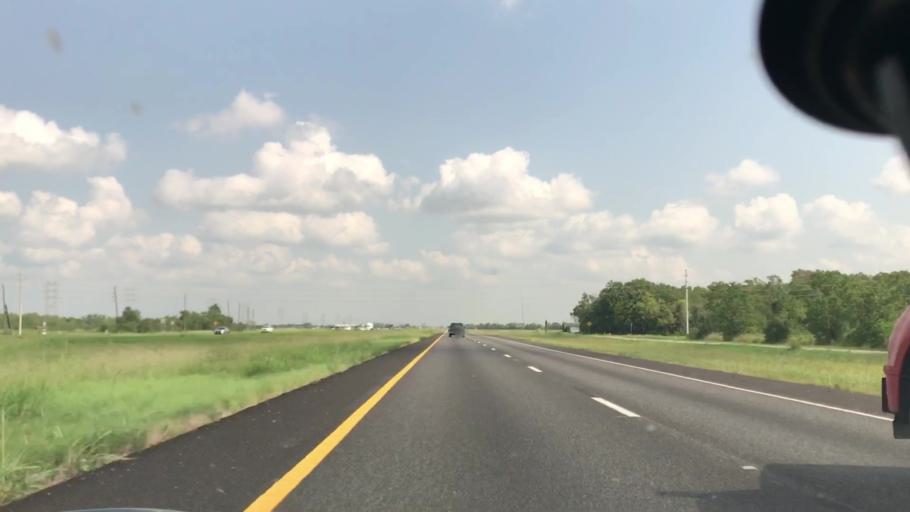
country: US
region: Texas
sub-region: Brazoria County
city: Rosharon
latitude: 29.4035
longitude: -95.4268
